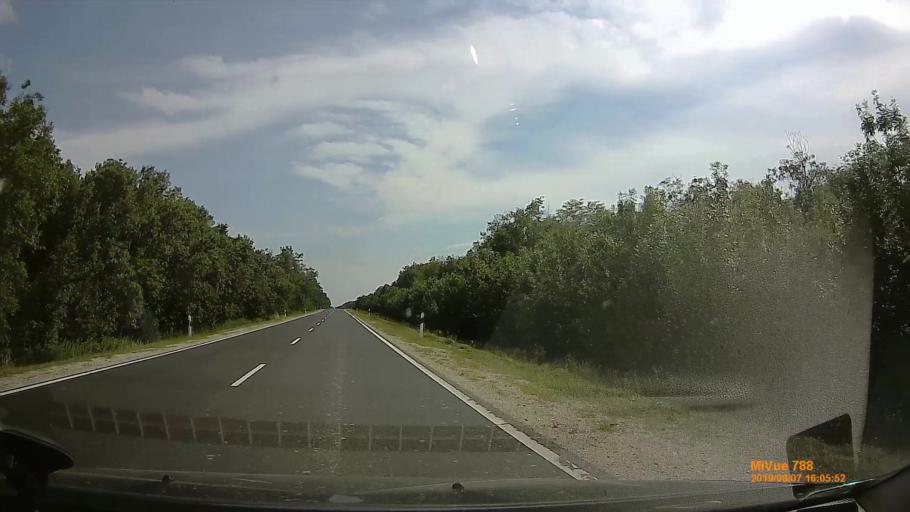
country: HU
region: Vas
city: Kormend
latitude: 46.9474
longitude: 16.6024
